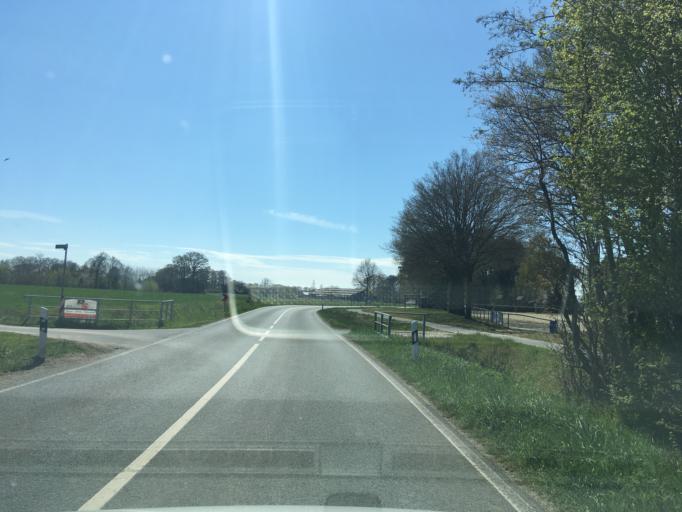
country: DE
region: North Rhine-Westphalia
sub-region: Regierungsbezirk Munster
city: Sudlohn
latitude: 51.9395
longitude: 6.8387
